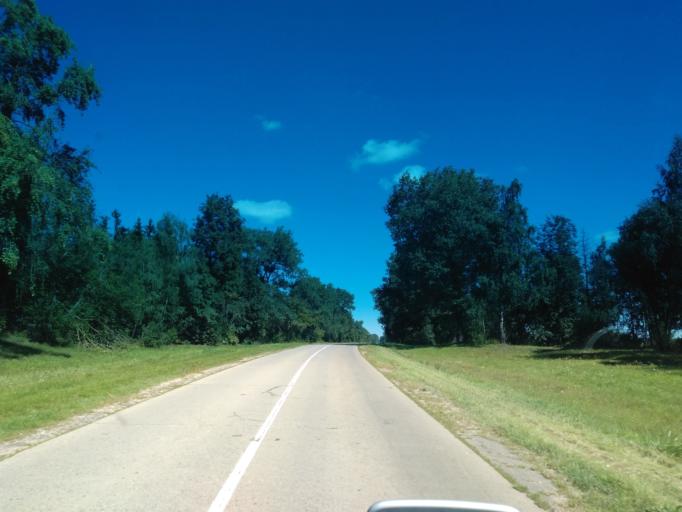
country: BY
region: Minsk
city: Stan'kava
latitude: 53.6430
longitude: 27.2934
